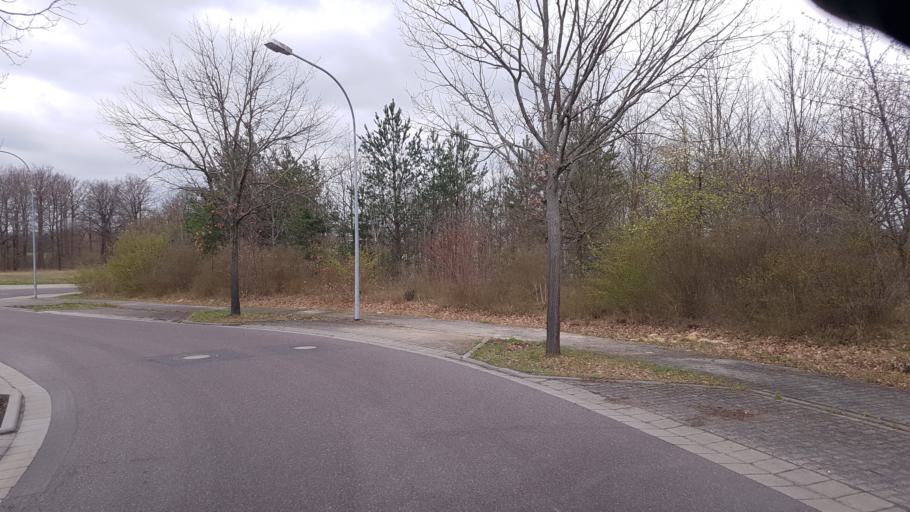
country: DE
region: Brandenburg
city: Schwarzheide
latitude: 51.4729
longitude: 13.8184
